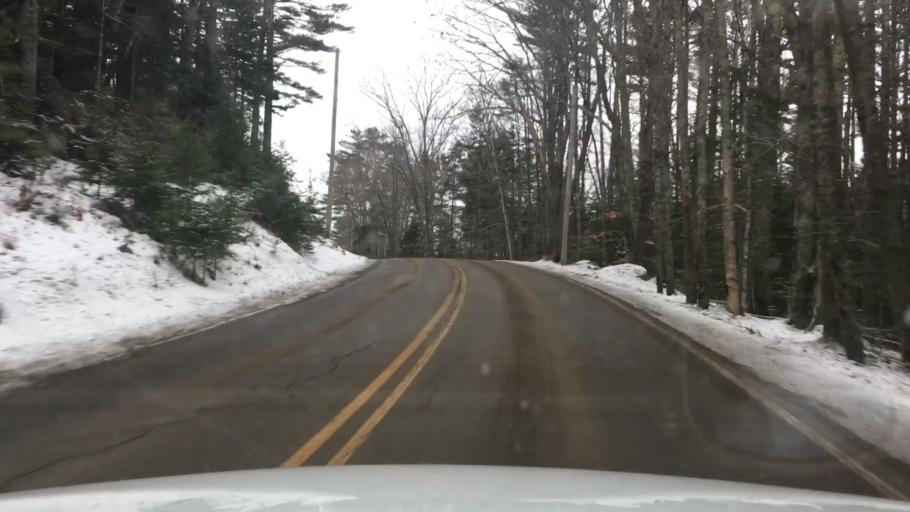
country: US
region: Maine
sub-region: Waldo County
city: Lincolnville
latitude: 44.2867
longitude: -69.0169
